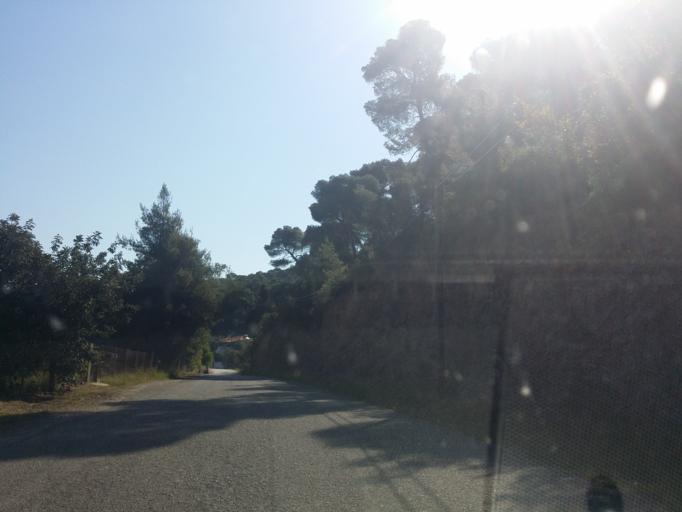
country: GR
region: Attica
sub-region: Nomos Piraios
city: Poros
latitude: 37.5206
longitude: 23.4669
